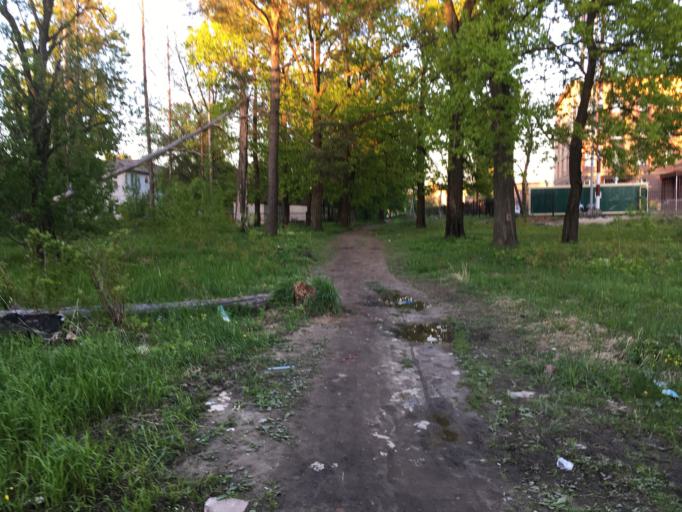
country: RU
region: Mariy-El
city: Yoshkar-Ola
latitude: 56.6298
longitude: 47.9344
